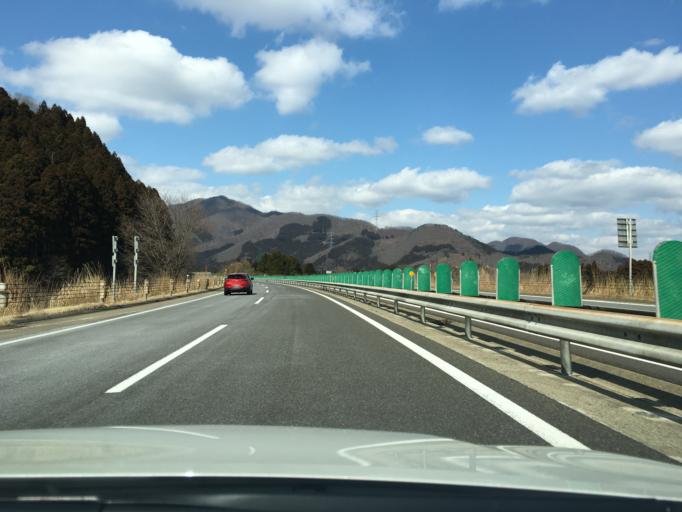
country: JP
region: Miyagi
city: Shiroishi
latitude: 38.1921
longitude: 140.5963
